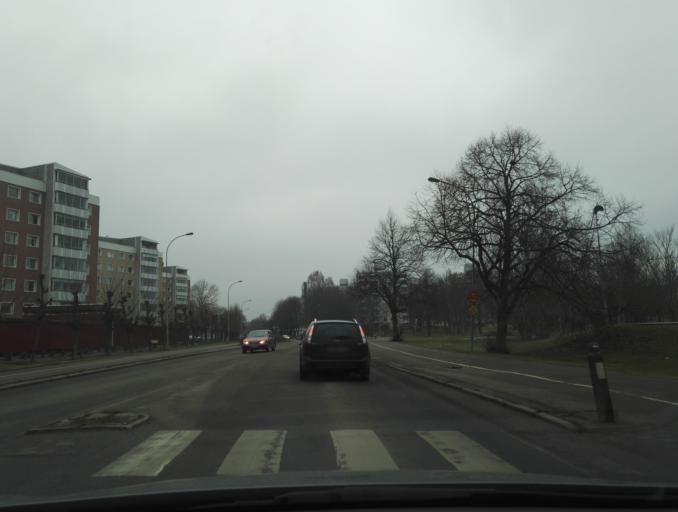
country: SE
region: Kronoberg
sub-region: Vaxjo Kommun
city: Vaexjoe
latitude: 56.8846
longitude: 14.8006
